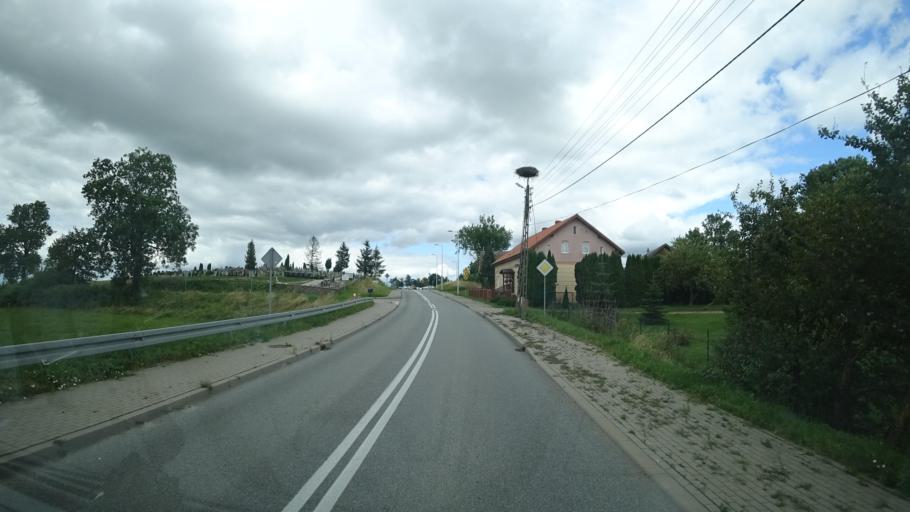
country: PL
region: Warmian-Masurian Voivodeship
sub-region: Powiat goldapski
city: Goldap
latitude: 54.2272
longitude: 22.2435
